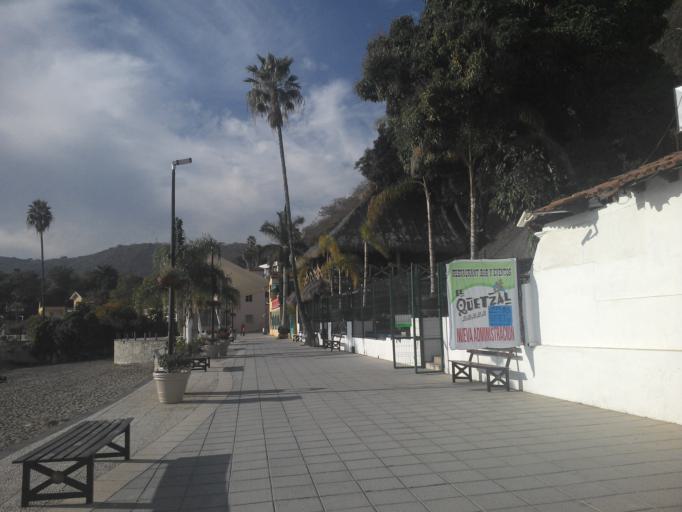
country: MX
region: Jalisco
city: Chapala
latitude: 20.2899
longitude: -103.1949
